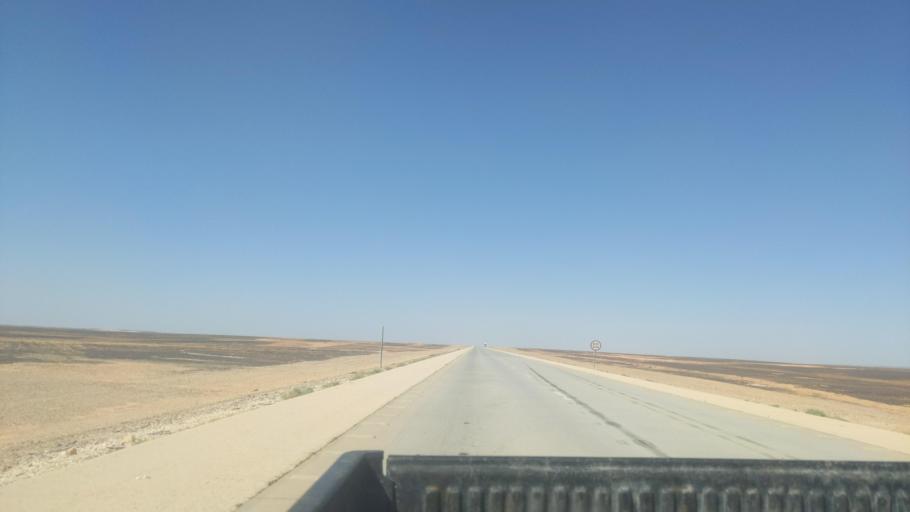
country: JO
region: Amman
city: Al Azraq ash Shamali
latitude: 31.4329
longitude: 36.7407
